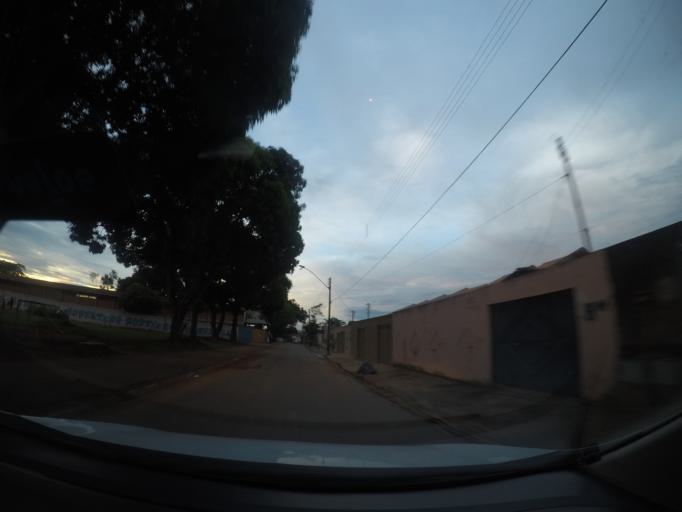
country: BR
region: Goias
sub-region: Goiania
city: Goiania
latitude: -16.7192
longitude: -49.3737
